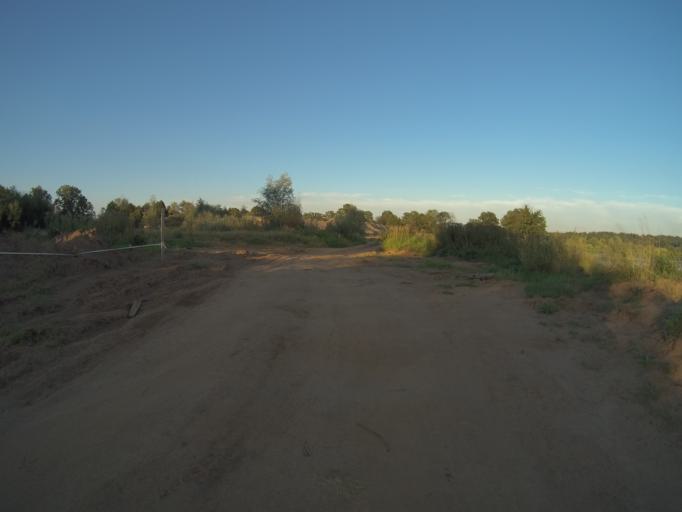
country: RU
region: Vladimir
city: Kommunar
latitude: 56.0860
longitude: 40.4173
